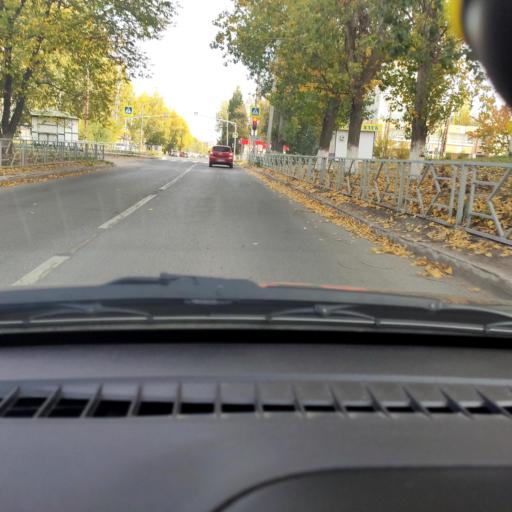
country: RU
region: Samara
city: Zhigulevsk
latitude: 53.4831
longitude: 49.4591
